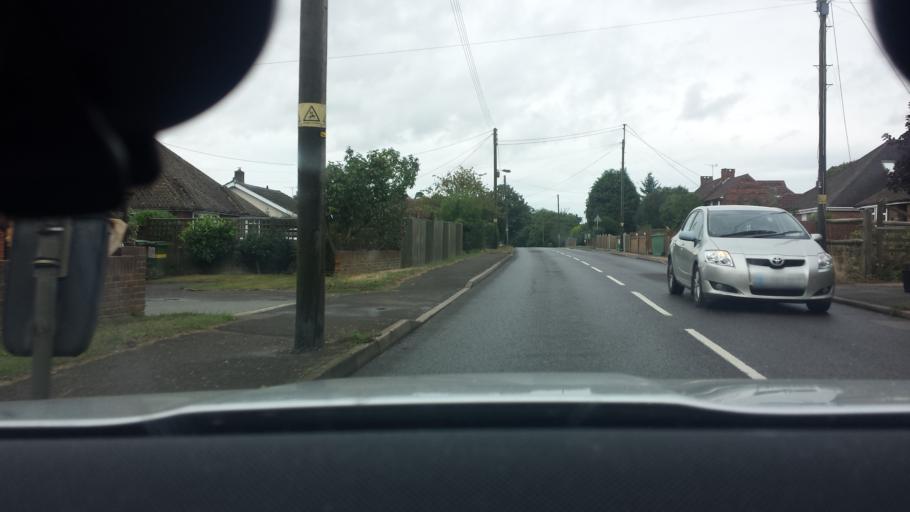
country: GB
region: England
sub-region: Kent
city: Headcorn
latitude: 51.2341
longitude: 0.5962
